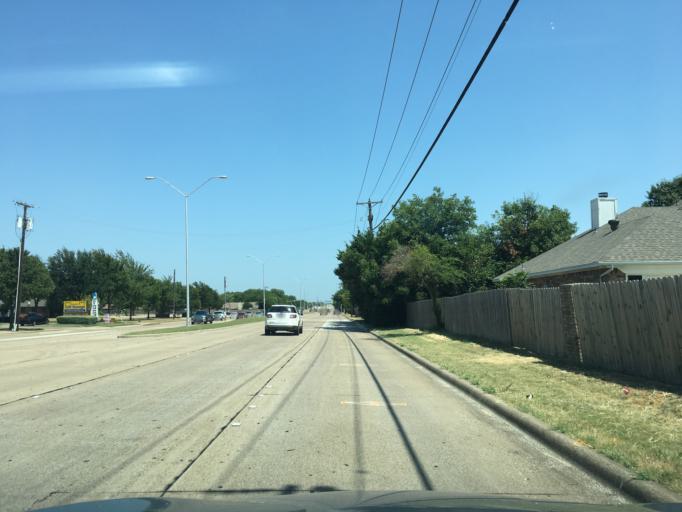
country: US
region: Texas
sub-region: Tarrant County
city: Edgecliff Village
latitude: 32.6348
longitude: -97.3659
